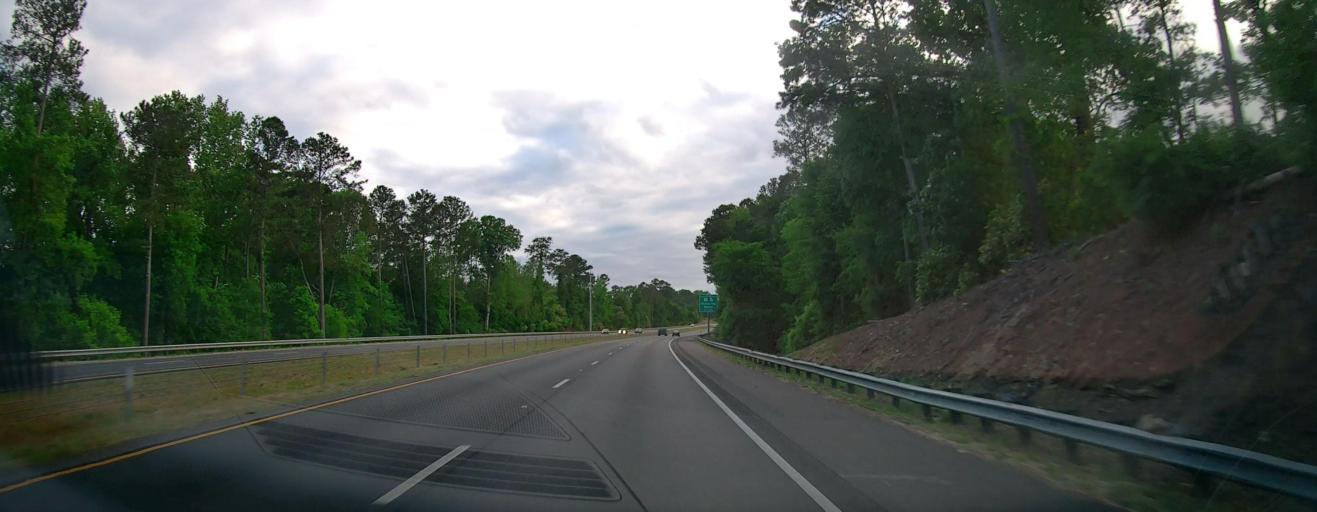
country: US
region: Georgia
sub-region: Clarke County
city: Country Club Estates
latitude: 33.9505
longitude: -83.4436
